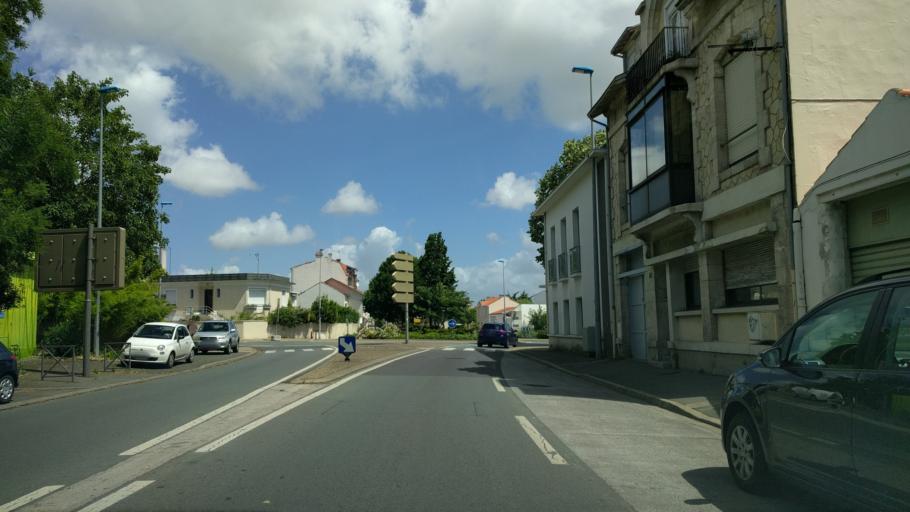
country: FR
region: Poitou-Charentes
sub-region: Departement de la Charente-Maritime
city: La Rochelle
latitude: 46.1610
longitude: -1.1402
